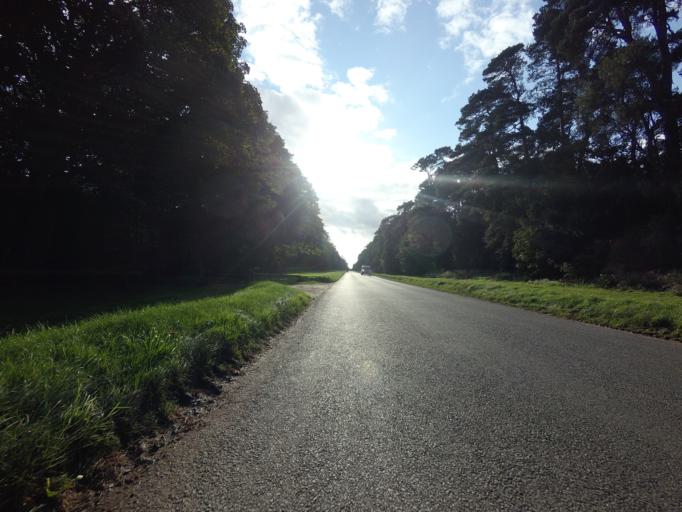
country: GB
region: England
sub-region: Norfolk
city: Dersingham
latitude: 52.8276
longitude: 0.5033
